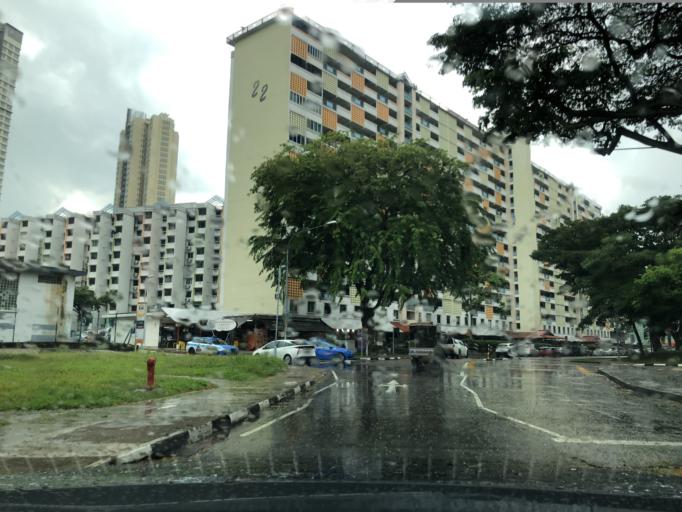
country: SG
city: Singapore
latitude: 1.2889
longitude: 103.8301
